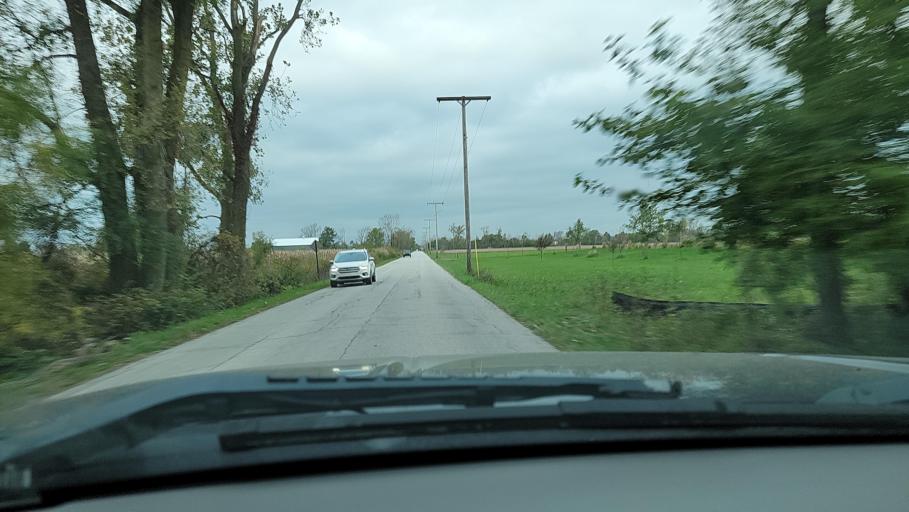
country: US
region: Indiana
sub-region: Porter County
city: South Haven
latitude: 41.5613
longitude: -87.1471
